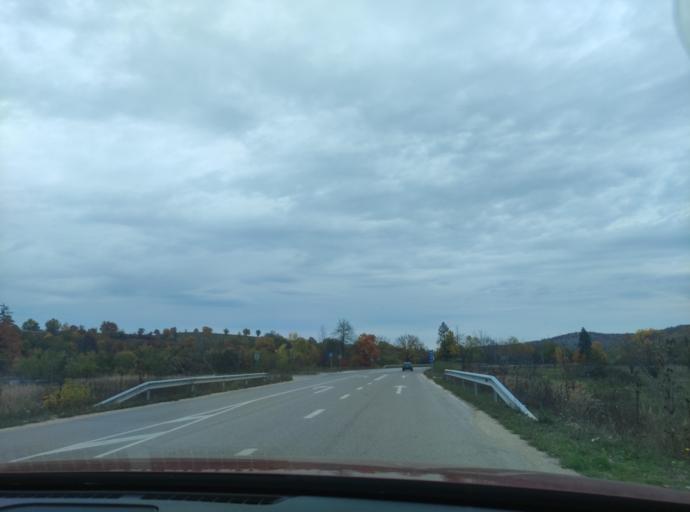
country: BG
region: Montana
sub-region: Obshtina Berkovitsa
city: Berkovitsa
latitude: 43.2515
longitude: 23.1684
